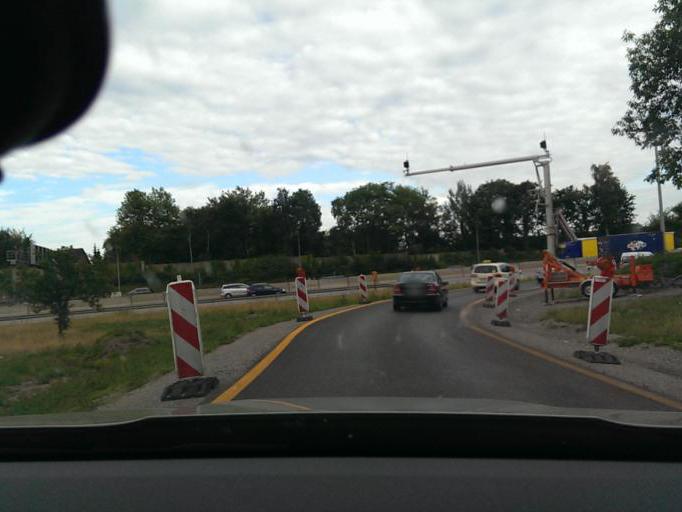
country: DE
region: Hamburg
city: Stellingen
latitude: 53.5944
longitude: 9.9211
